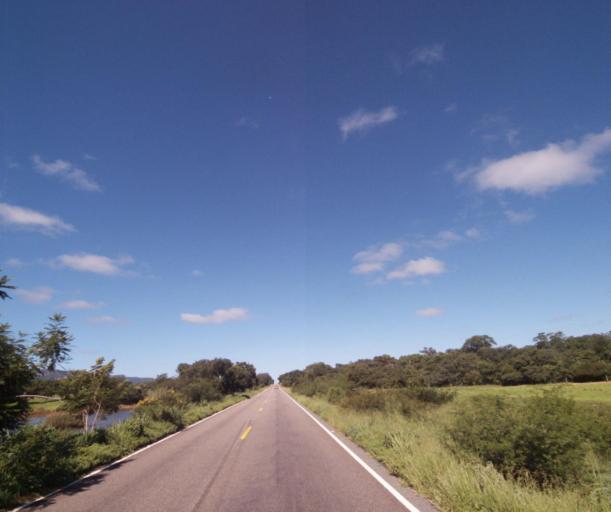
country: BR
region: Bahia
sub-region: Palmas De Monte Alto
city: Palmas de Monte Alto
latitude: -14.2425
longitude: -43.0757
